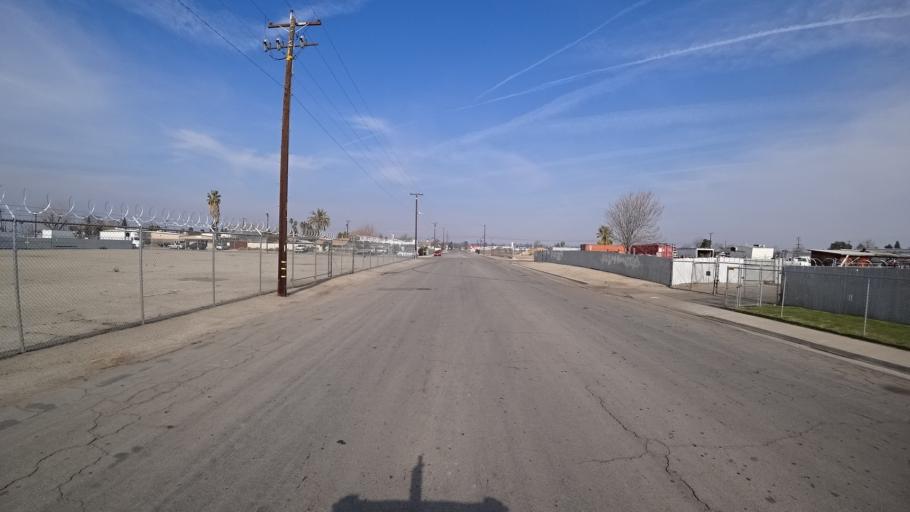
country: US
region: California
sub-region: Kern County
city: Bakersfield
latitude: 35.3707
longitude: -118.9985
